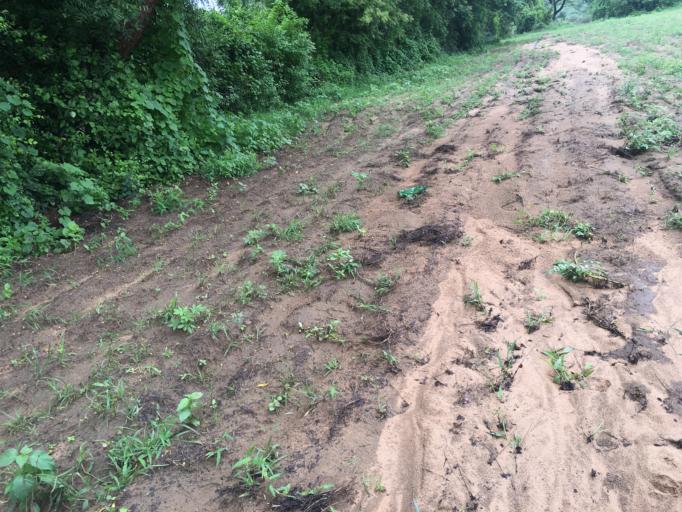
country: IN
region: Gujarat
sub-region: Mahesana
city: Kadi
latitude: 23.1615
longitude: 72.3768
